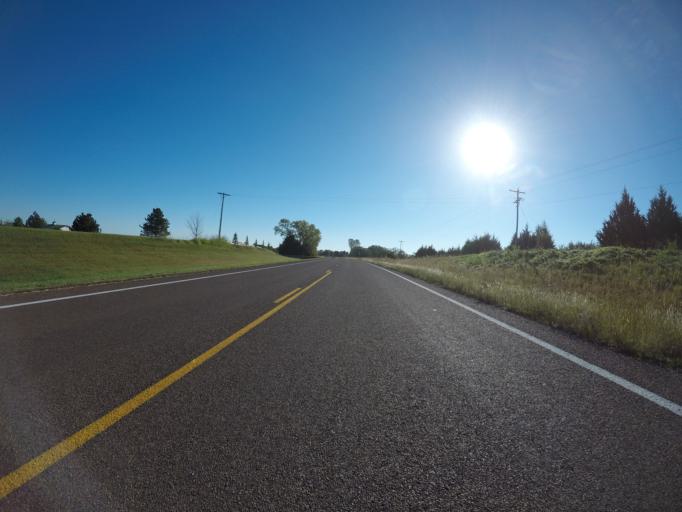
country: US
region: Kansas
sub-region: Douglas County
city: Eudora
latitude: 39.0009
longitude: -95.0604
